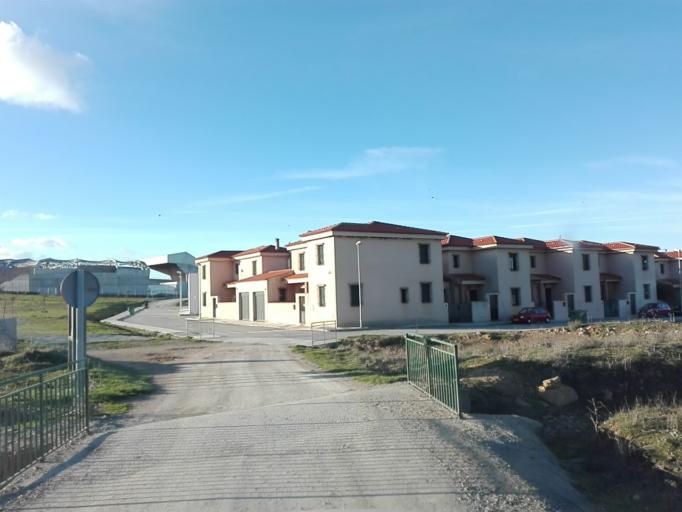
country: ES
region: Extremadura
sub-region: Provincia de Badajoz
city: Llerena
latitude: 38.2311
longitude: -6.0145
